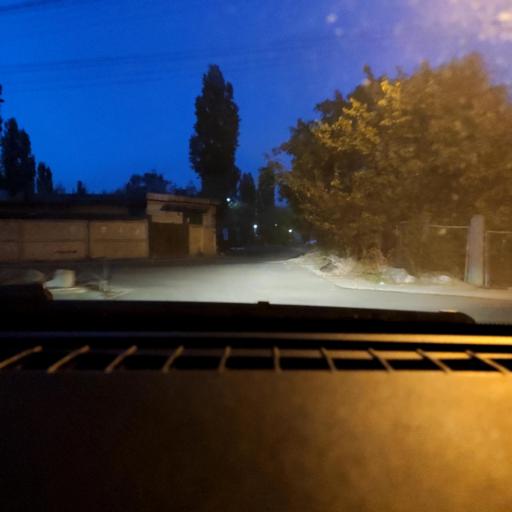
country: RU
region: Voronezj
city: Voronezh
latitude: 51.6739
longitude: 39.2657
